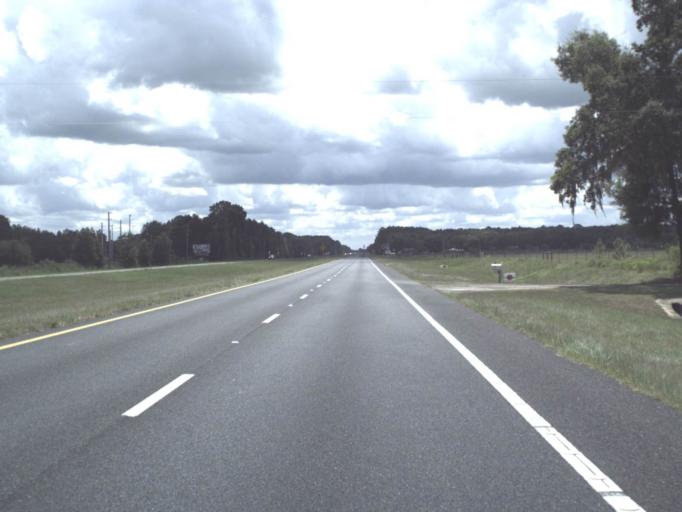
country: US
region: Florida
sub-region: Levy County
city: Williston
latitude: 29.3985
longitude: -82.4989
